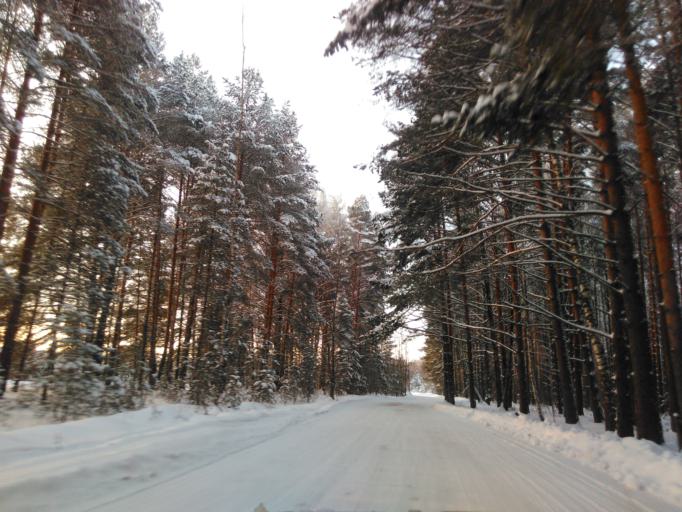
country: RU
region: Tverskaya
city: Konakovo
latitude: 56.6548
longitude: 36.6583
